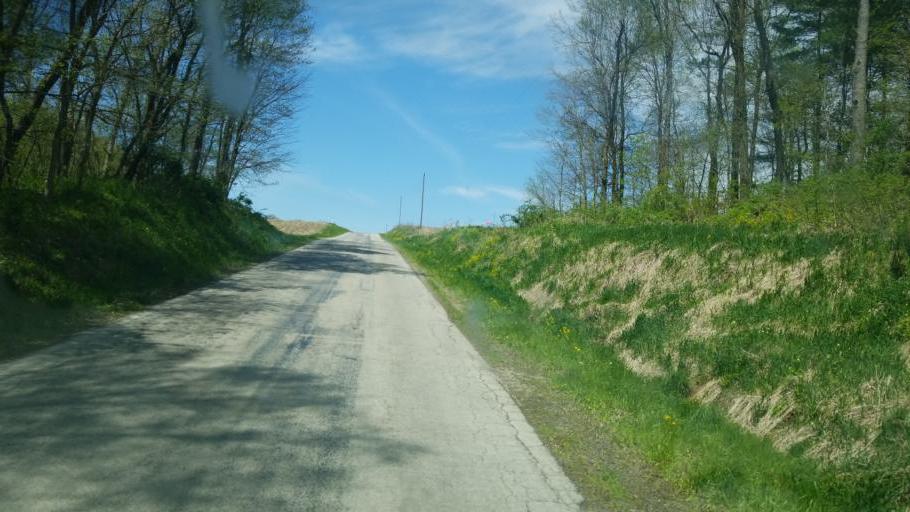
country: US
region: Ohio
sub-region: Wayne County
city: Shreve
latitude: 40.7720
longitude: -82.1173
